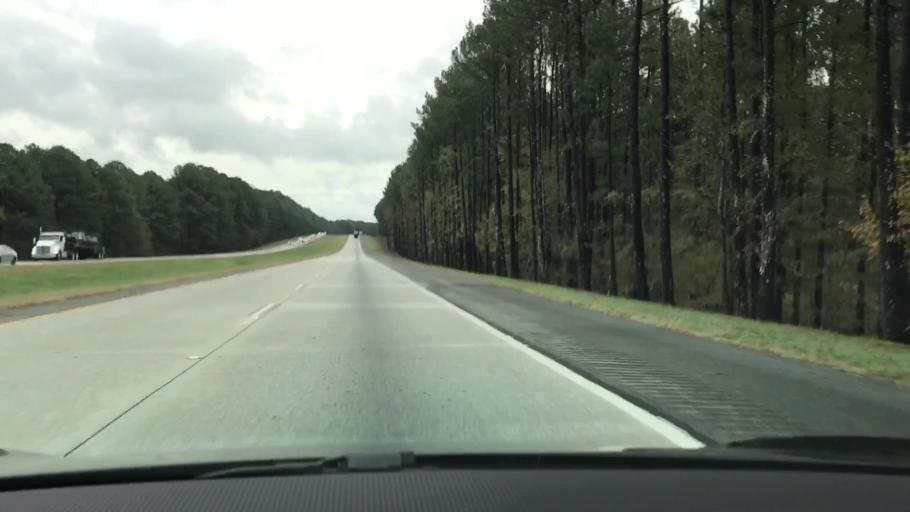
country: US
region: Georgia
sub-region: Taliaferro County
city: Crawfordville
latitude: 33.5259
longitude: -82.8855
